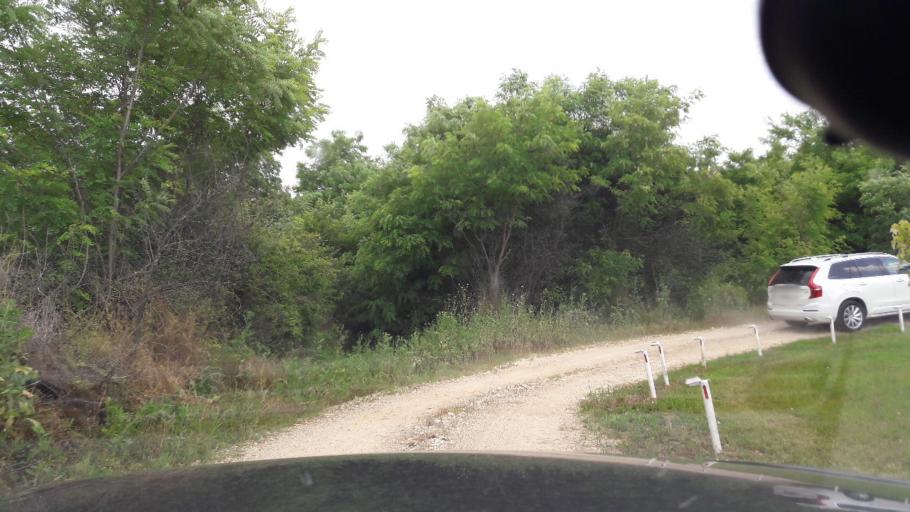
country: RS
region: Central Serbia
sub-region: Belgrade
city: Sopot
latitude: 44.6014
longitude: 20.5989
